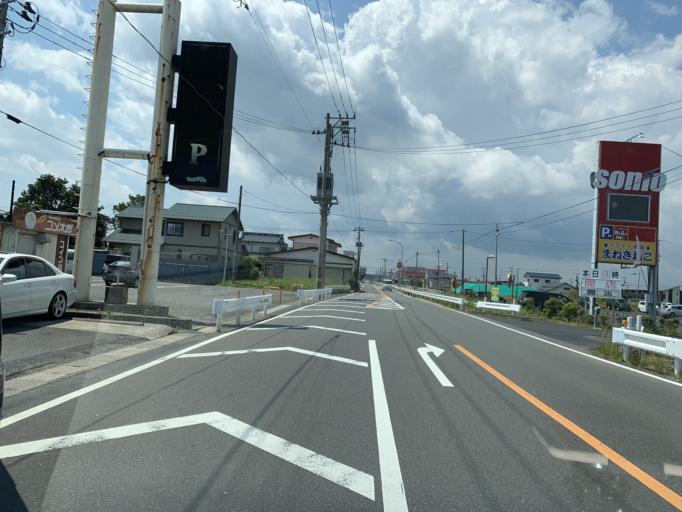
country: JP
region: Miyagi
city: Wakuya
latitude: 38.4645
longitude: 141.0918
